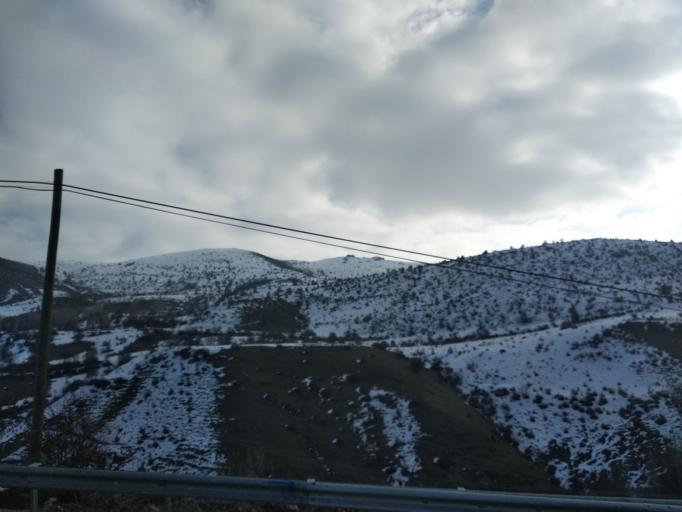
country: TR
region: Gumushane
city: Kelkit
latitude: 40.0723
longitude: 39.4971
